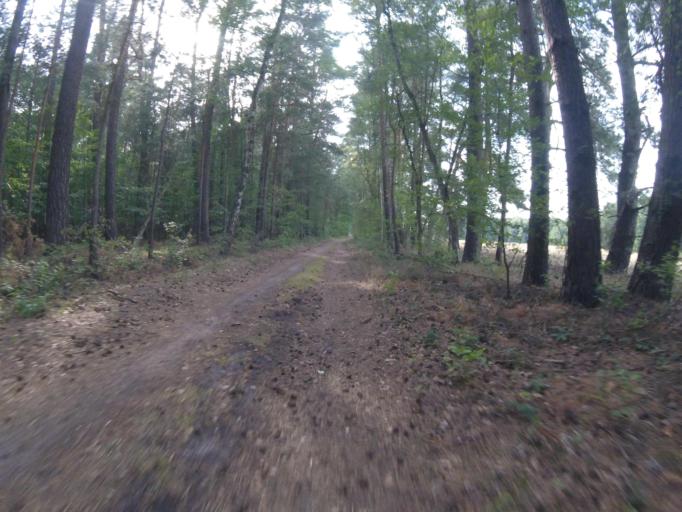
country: DE
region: Brandenburg
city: Bestensee
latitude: 52.2394
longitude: 13.7589
